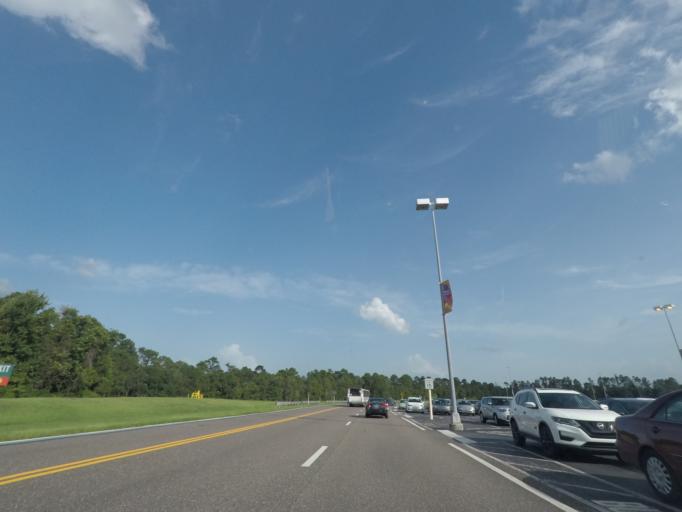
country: US
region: Florida
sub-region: Osceola County
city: Celebration
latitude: 28.3521
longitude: -81.5847
